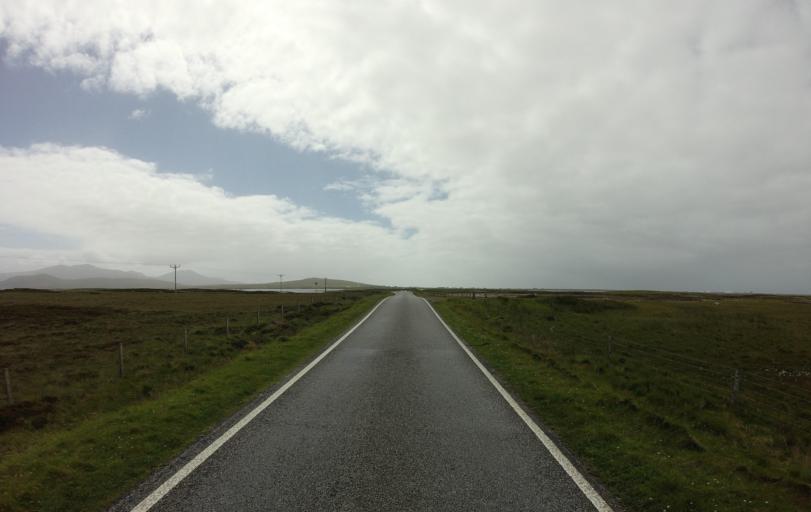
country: GB
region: Scotland
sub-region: Eilean Siar
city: Benbecula
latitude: 57.3681
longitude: -7.3508
